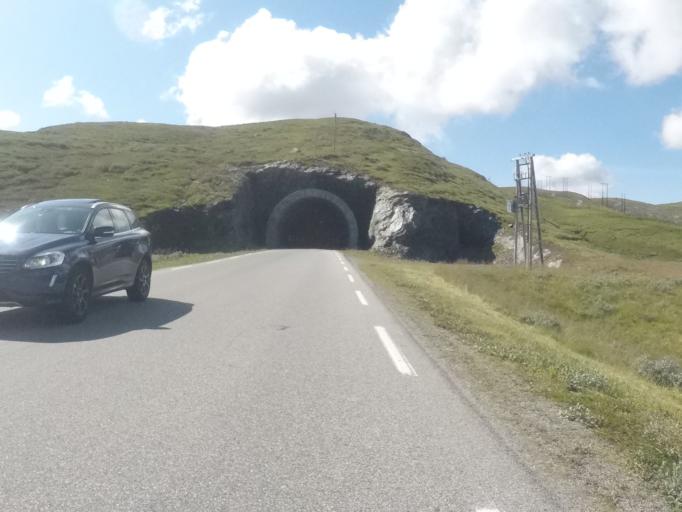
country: NO
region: Sogn og Fjordane
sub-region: Vik
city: Vik
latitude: 61.0124
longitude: 6.5418
